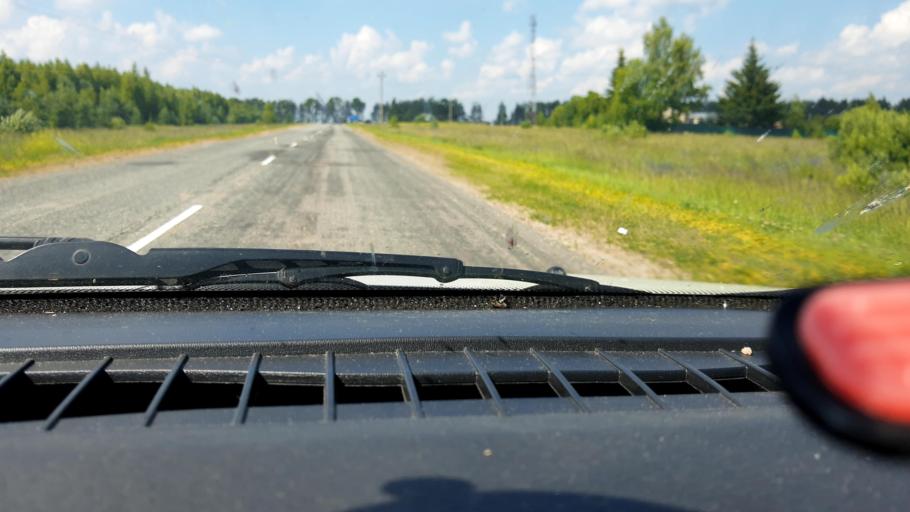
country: RU
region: Nizjnij Novgorod
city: Tonkino
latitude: 57.3678
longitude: 46.4224
